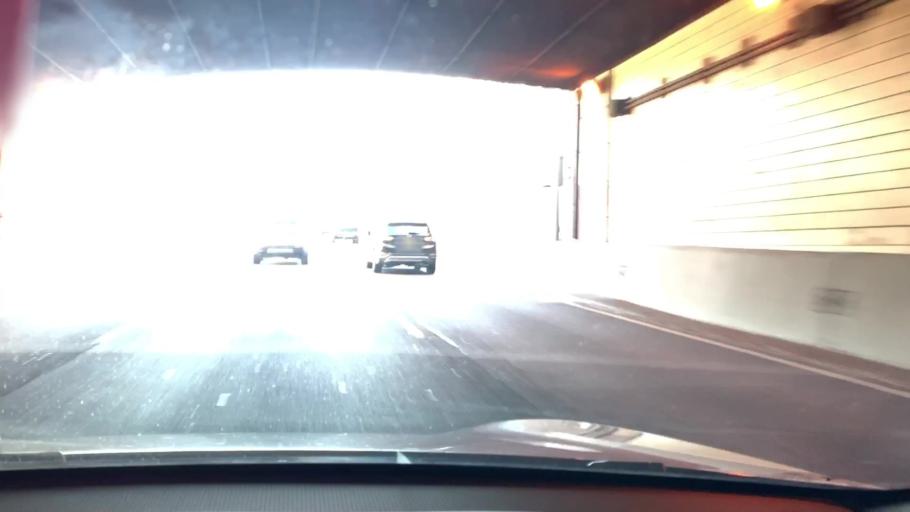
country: US
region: New York
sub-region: Bronx
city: The Bronx
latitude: 40.8331
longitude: -73.8602
